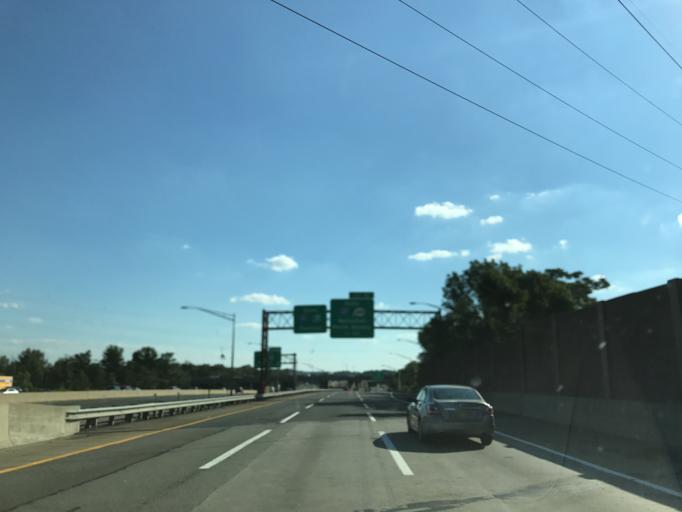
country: US
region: New Jersey
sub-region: Middlesex County
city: Fords
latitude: 40.5309
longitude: -74.3337
